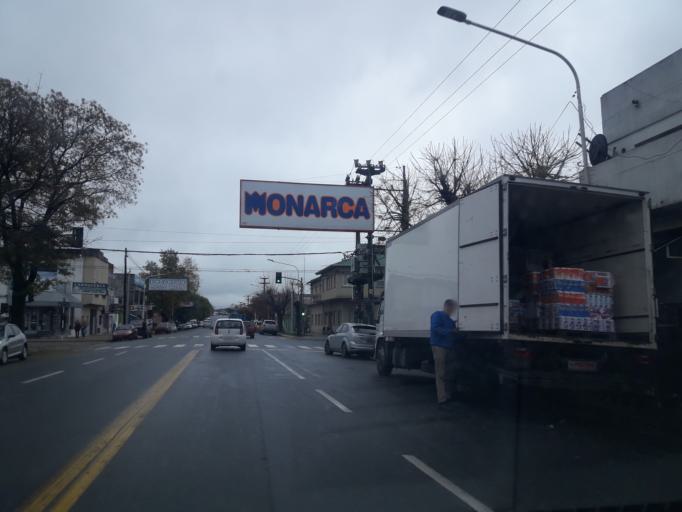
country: AR
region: Buenos Aires
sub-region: Partido de Tandil
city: Tandil
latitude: -37.3215
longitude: -59.1497
